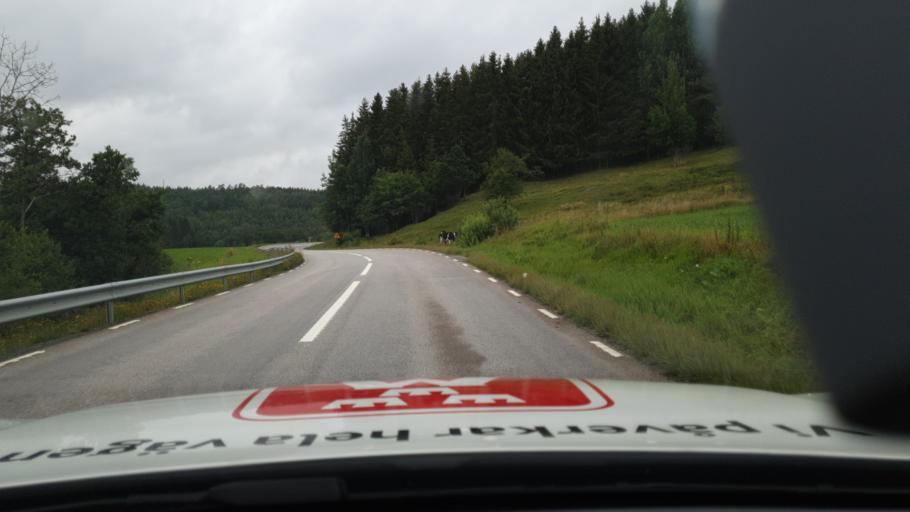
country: SE
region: Vaestra Goetaland
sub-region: Lilla Edets Kommun
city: Lilla Edet
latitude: 58.1513
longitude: 12.0592
